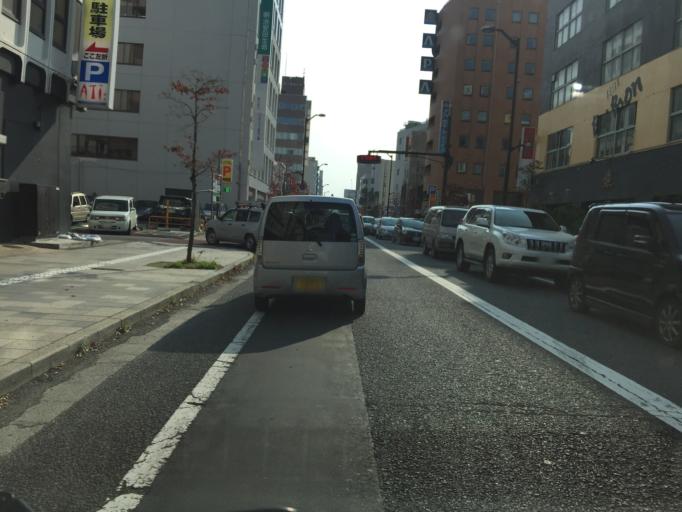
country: JP
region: Fukushima
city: Koriyama
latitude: 37.3968
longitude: 140.3871
